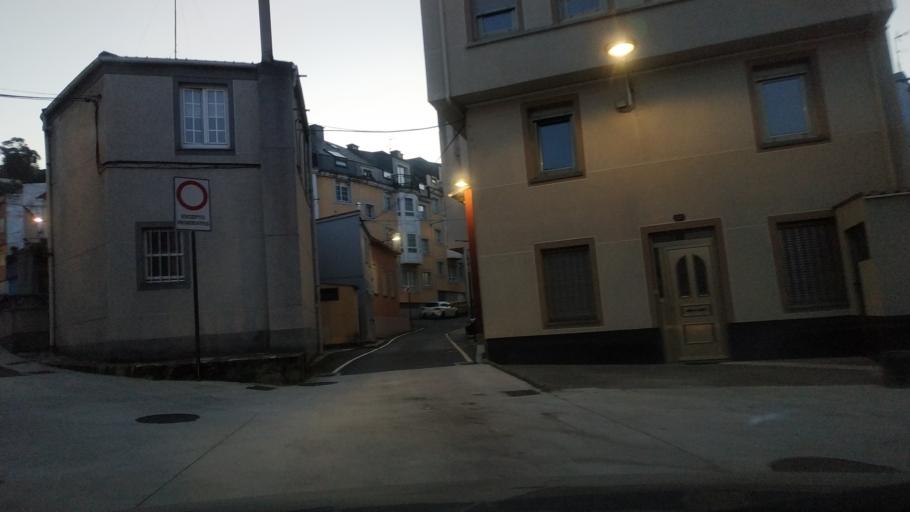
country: ES
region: Galicia
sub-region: Provincia da Coruna
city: Culleredo
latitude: 43.3278
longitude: -8.3933
